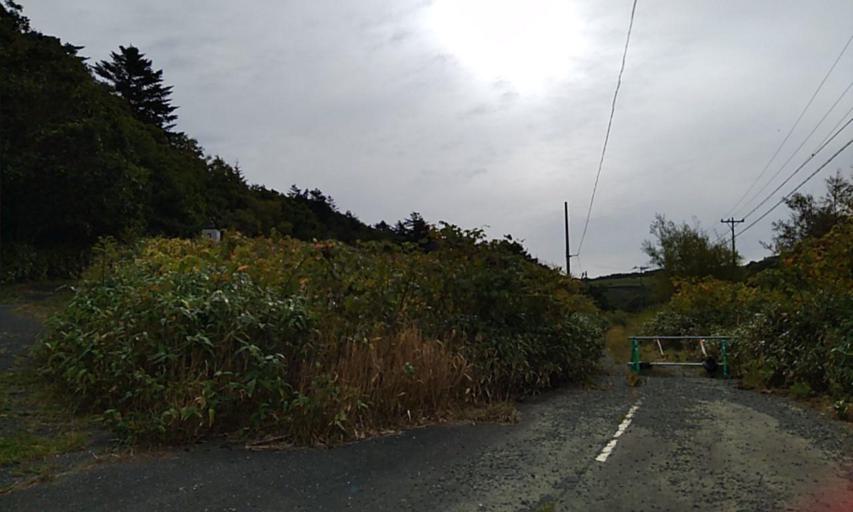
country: JP
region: Hokkaido
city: Makubetsu
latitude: 45.4851
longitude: 141.8848
